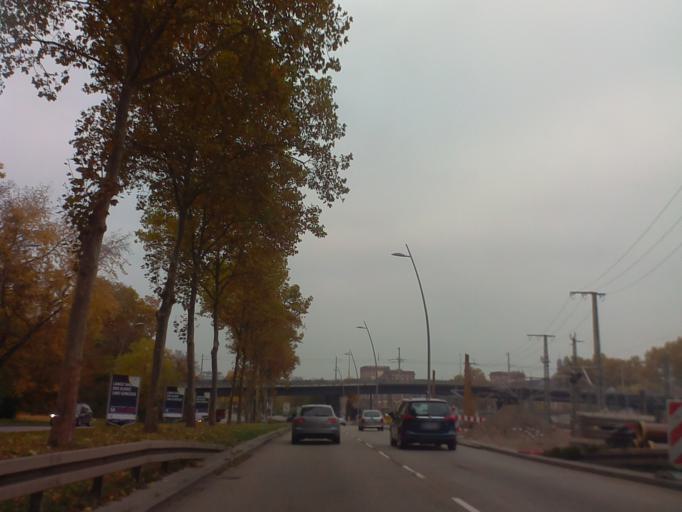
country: DE
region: Baden-Wuerttemberg
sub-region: Karlsruhe Region
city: Mannheim
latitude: 49.4791
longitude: 8.4678
